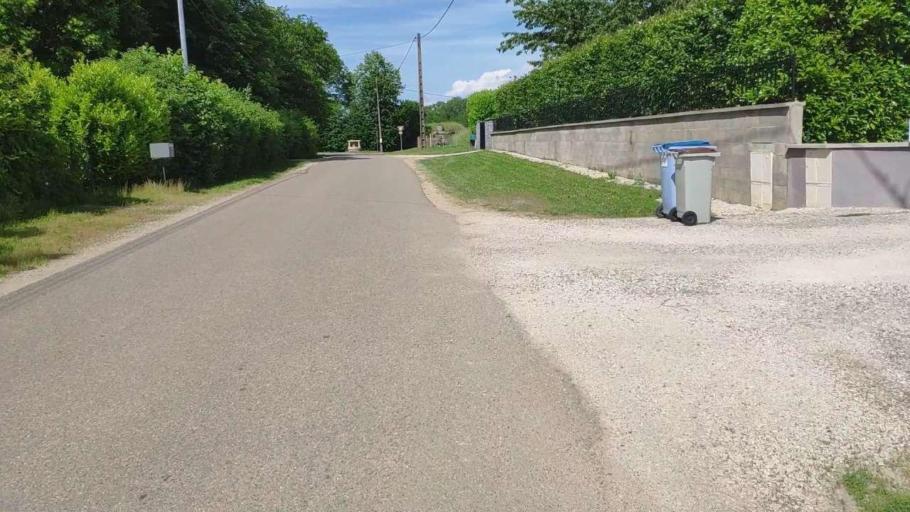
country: FR
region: Franche-Comte
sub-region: Departement du Jura
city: Bletterans
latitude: 46.7261
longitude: 5.4994
